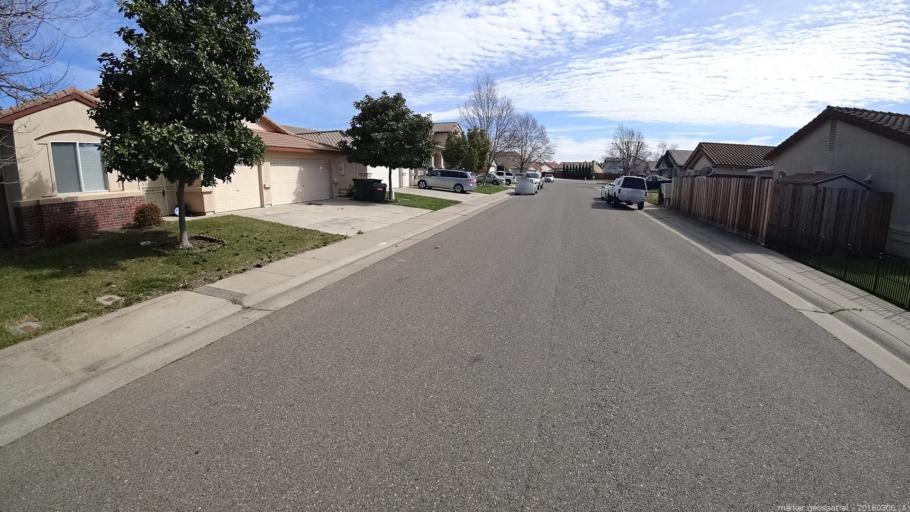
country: US
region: California
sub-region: Sacramento County
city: Vineyard
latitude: 38.4660
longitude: -121.3496
